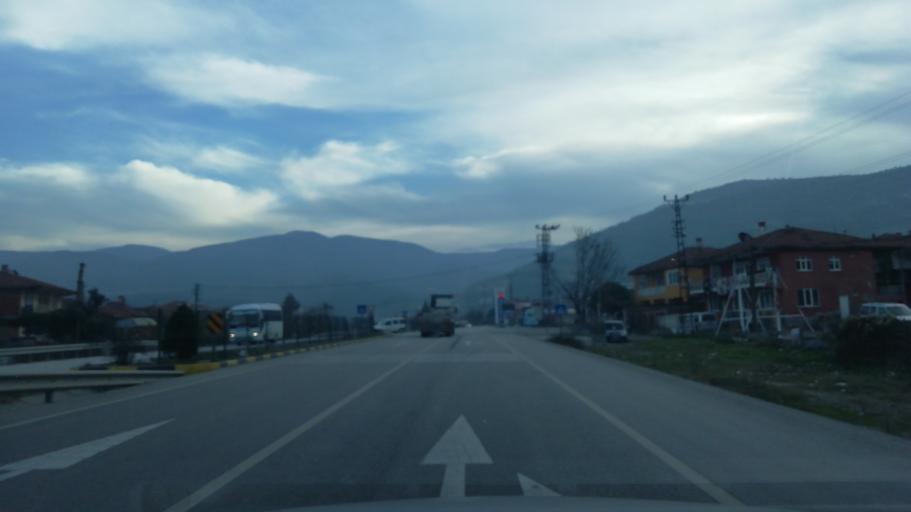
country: TR
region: Karabuk
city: Karabuk
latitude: 41.1048
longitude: 32.6690
